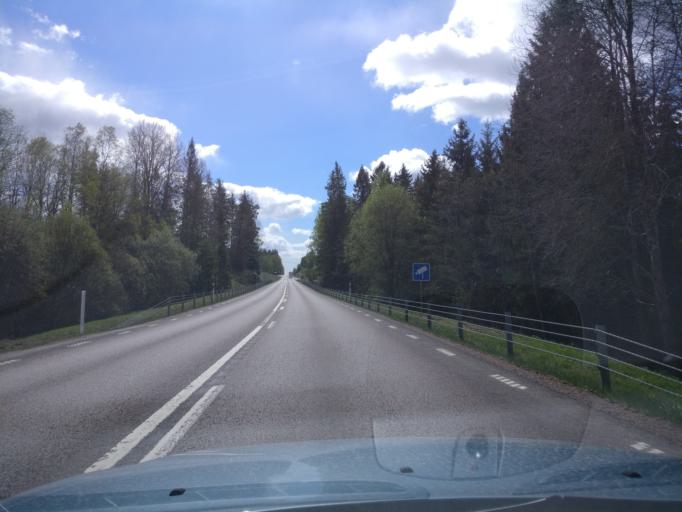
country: SE
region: Vaermland
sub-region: Karlstads Kommun
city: Molkom
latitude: 59.5368
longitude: 13.6189
